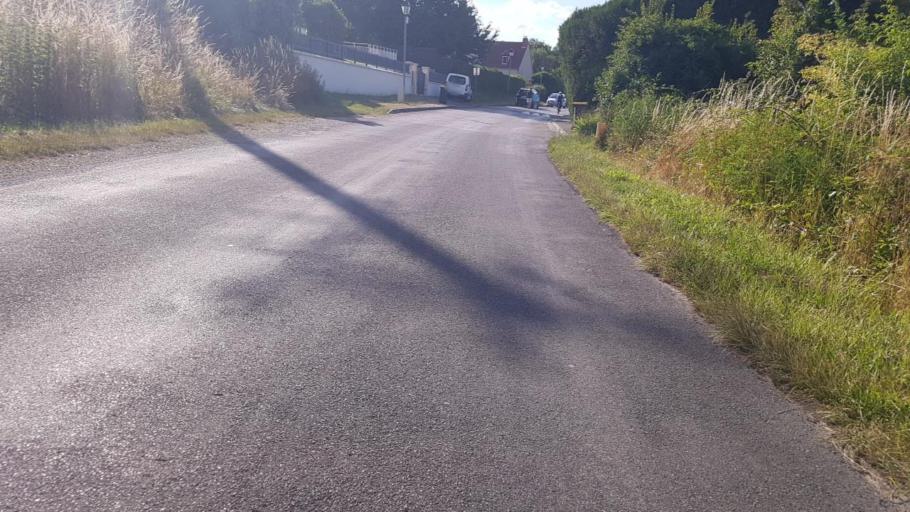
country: FR
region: Picardie
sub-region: Departement de l'Oise
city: Senlis
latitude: 49.1977
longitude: 2.5973
